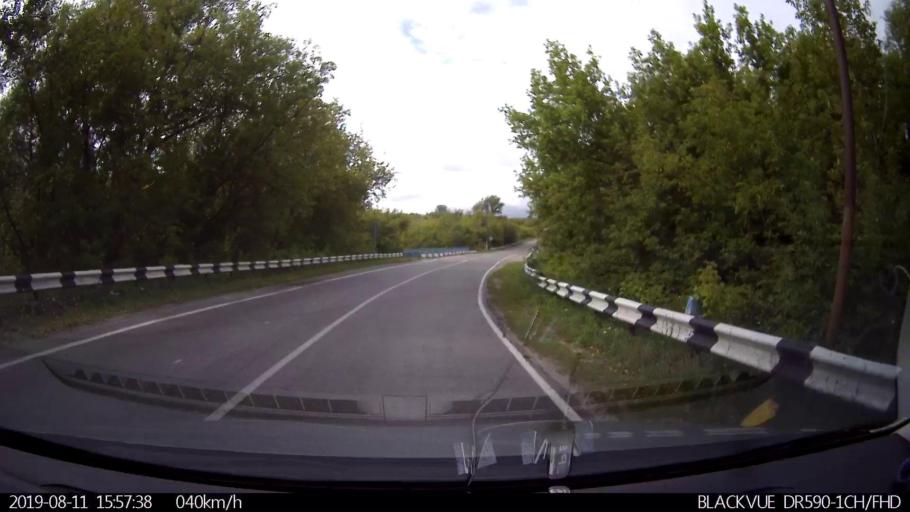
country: RU
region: Ulyanovsk
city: Ignatovka
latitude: 53.9517
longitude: 47.6519
